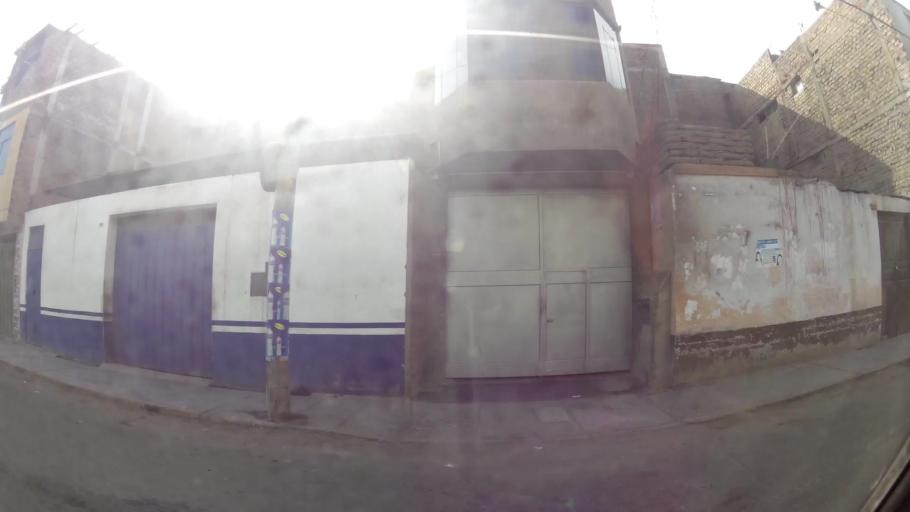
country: PE
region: La Libertad
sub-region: Provincia de Trujillo
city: Trujillo
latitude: -8.1044
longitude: -79.0177
